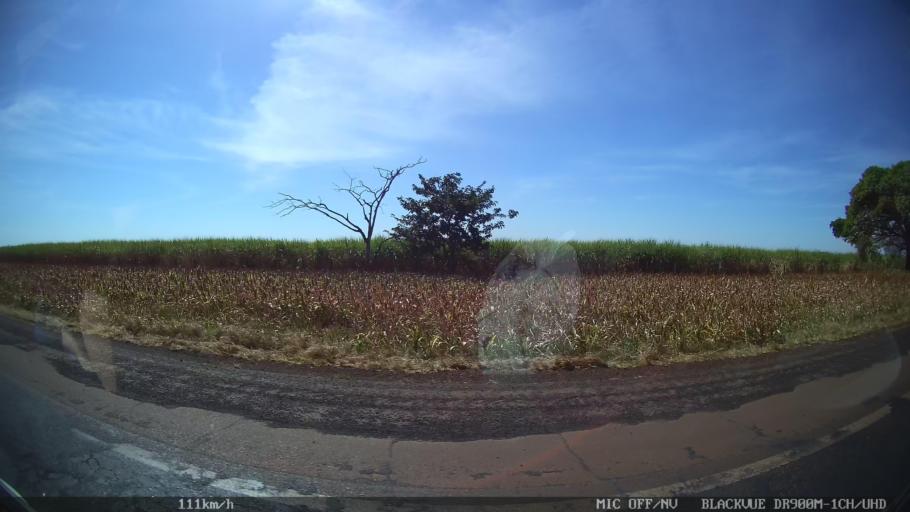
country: BR
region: Sao Paulo
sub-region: Ipua
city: Ipua
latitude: -20.4881
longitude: -48.0603
